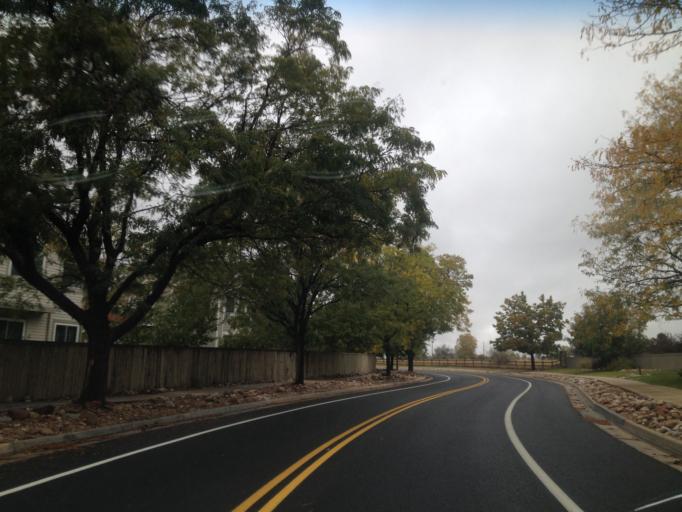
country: US
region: Colorado
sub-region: Boulder County
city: Superior
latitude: 39.9776
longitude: -105.1629
